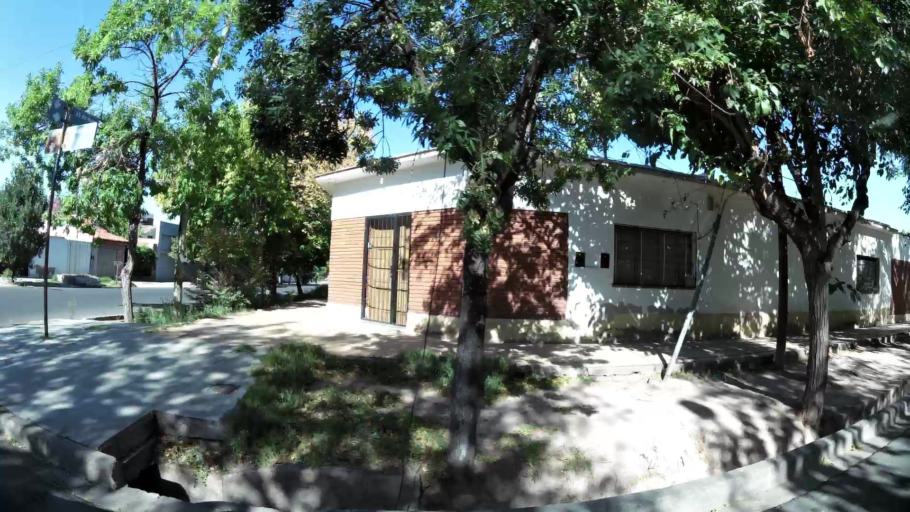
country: AR
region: Mendoza
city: Mendoza
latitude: -32.8990
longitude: -68.8177
